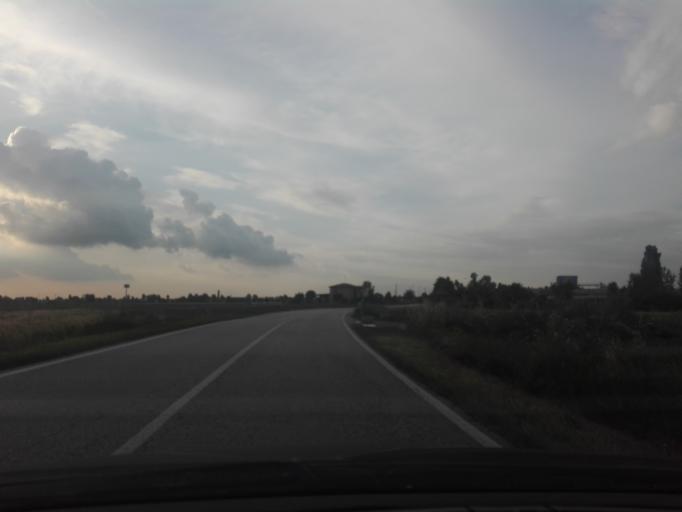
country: IT
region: Veneto
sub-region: Provincia di Rovigo
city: Lama Pezzoli
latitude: 45.0553
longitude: 11.9037
